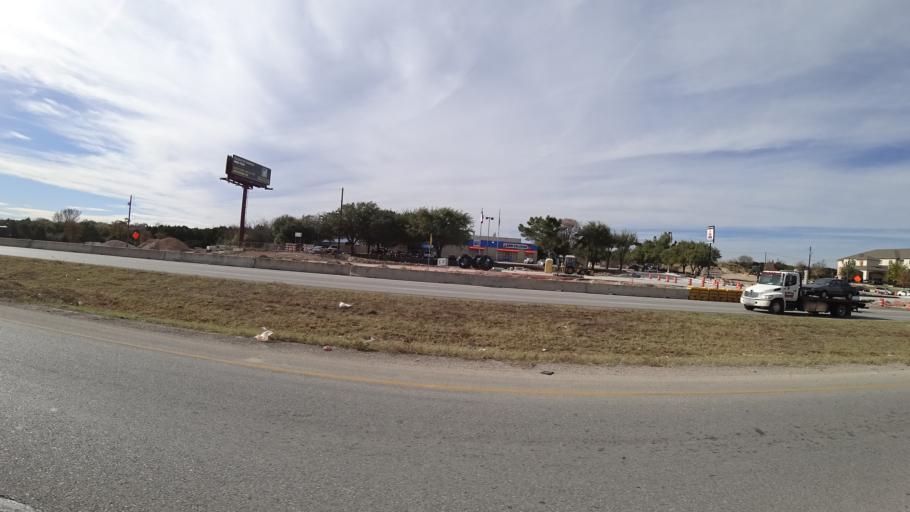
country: US
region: Texas
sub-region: Travis County
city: Austin
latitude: 30.2912
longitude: -97.6638
